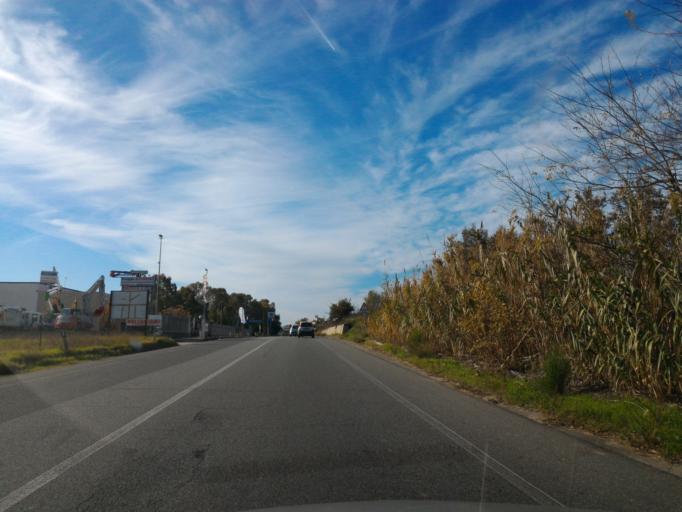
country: IT
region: Calabria
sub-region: Provincia di Catanzaro
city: Sellia Marina
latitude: 38.8906
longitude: 16.7196
